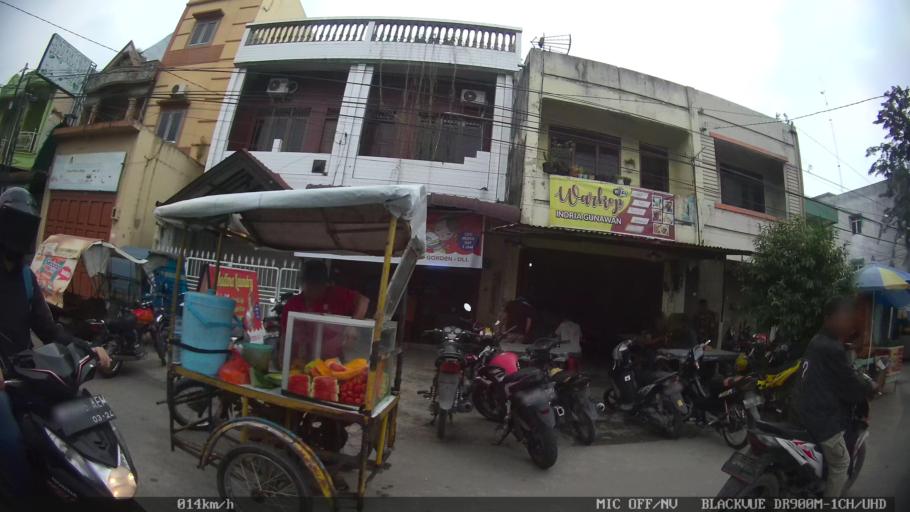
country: ID
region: North Sumatra
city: Medan
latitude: 3.5822
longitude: 98.7075
